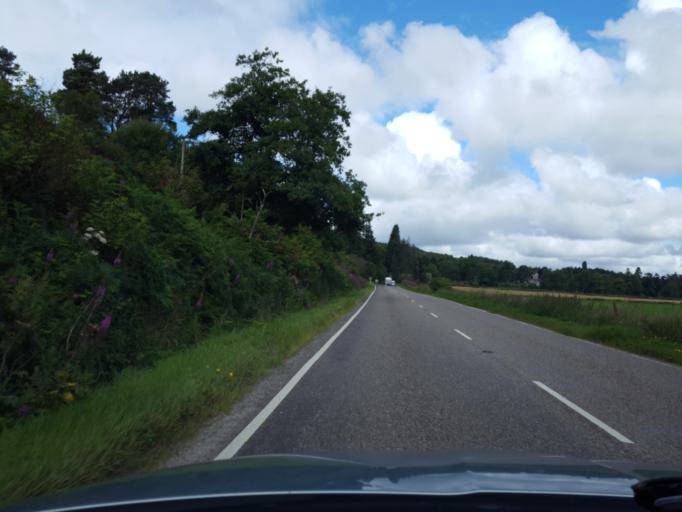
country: GB
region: Scotland
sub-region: Moray
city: Rothes
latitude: 57.5508
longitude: -3.2406
